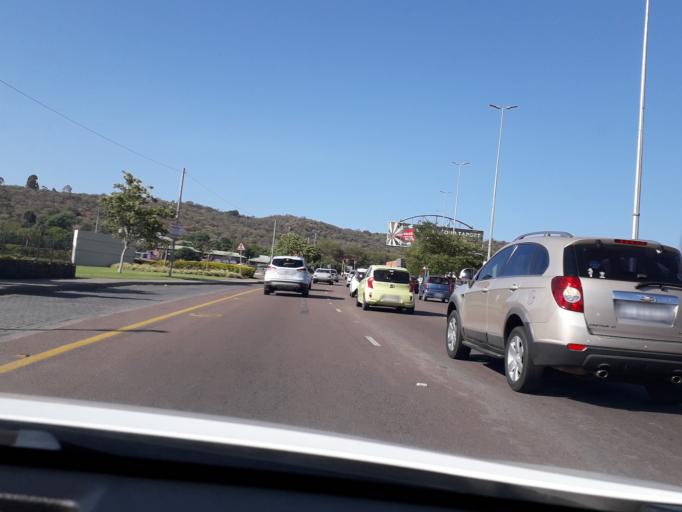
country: ZA
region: Gauteng
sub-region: City of Tshwane Metropolitan Municipality
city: Pretoria
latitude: -25.7648
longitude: 28.3225
